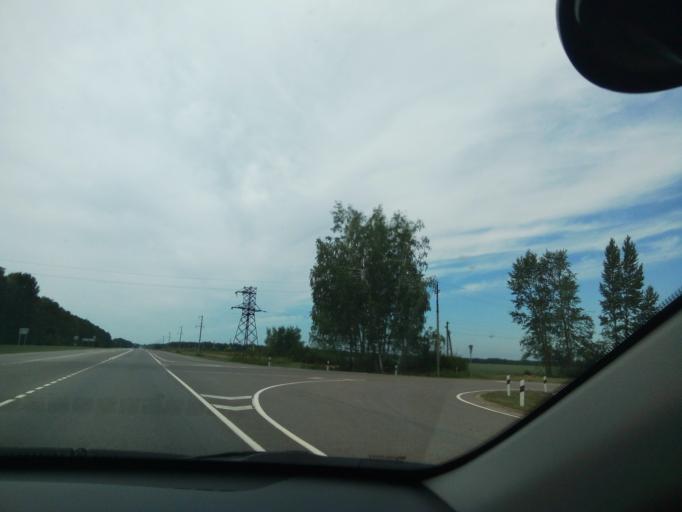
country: RU
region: Tambov
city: Selezni
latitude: 52.6653
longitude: 41.0882
